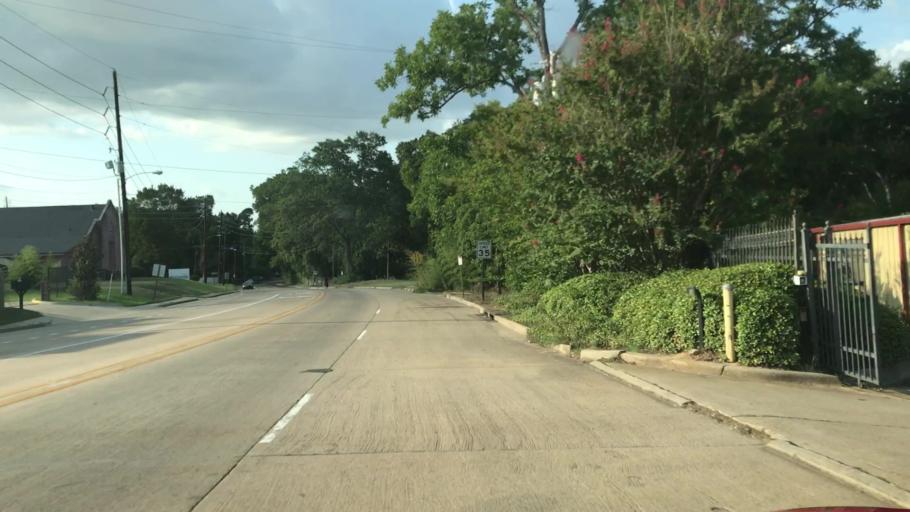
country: US
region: Louisiana
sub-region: Bossier Parish
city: Bossier City
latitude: 32.4552
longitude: -93.7544
